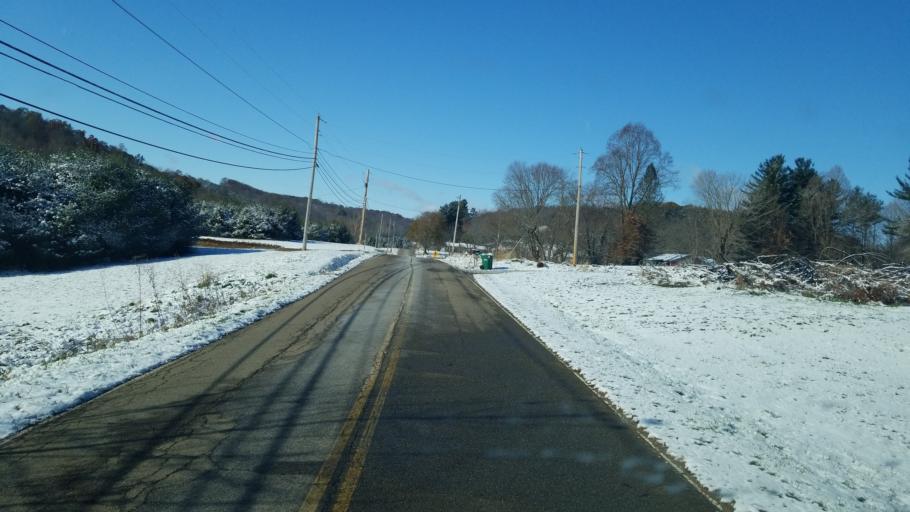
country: US
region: Ohio
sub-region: Licking County
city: Newark
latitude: 40.1615
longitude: -82.3481
